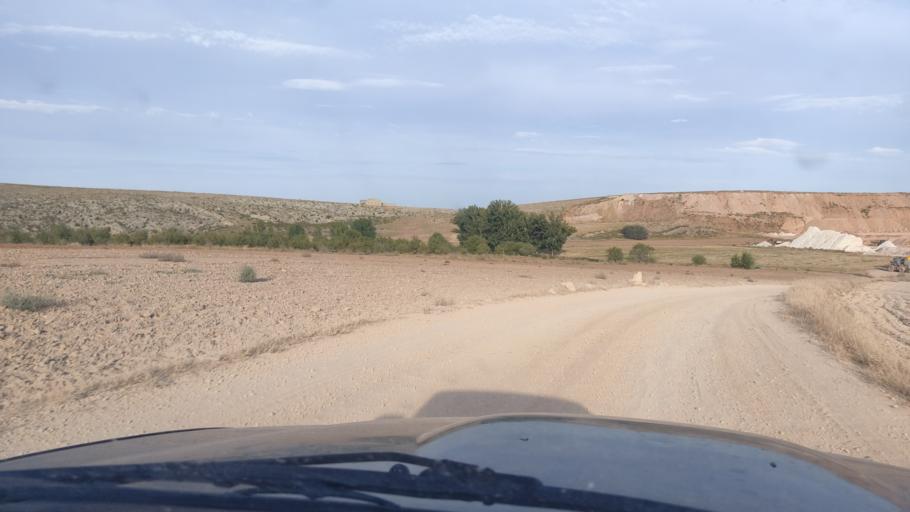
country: ES
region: Aragon
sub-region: Provincia de Teruel
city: Monforte de Moyuela
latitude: 41.0459
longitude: -0.9810
